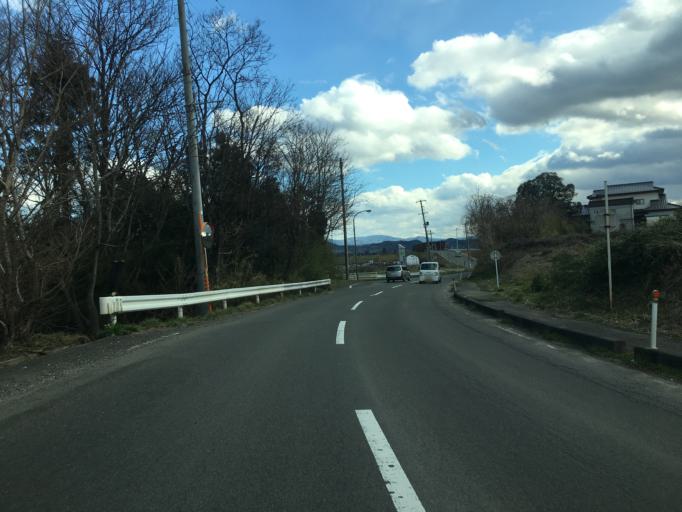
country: JP
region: Fukushima
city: Yanagawamachi-saiwaicho
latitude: 37.8668
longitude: 140.5679
